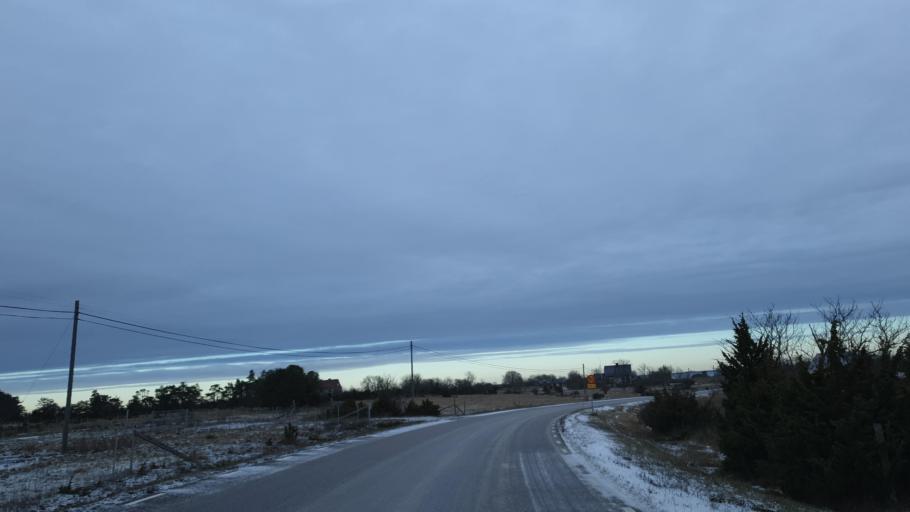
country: SE
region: Gotland
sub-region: Gotland
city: Slite
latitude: 57.4224
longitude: 18.8980
